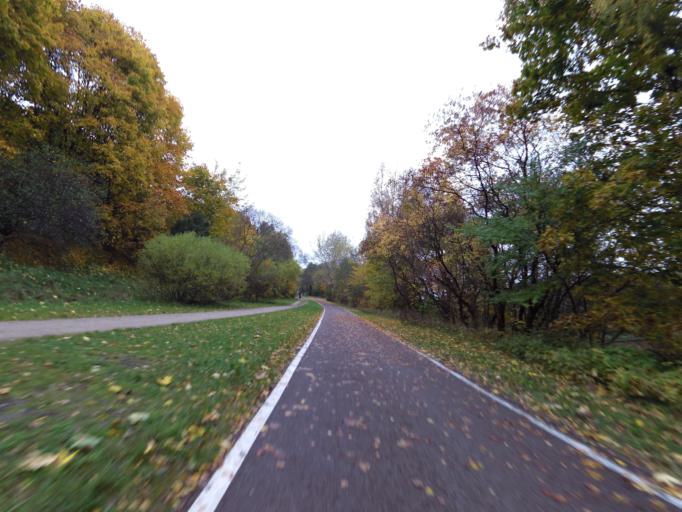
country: LT
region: Vilnius County
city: Rasos
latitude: 54.7169
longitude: 25.3111
